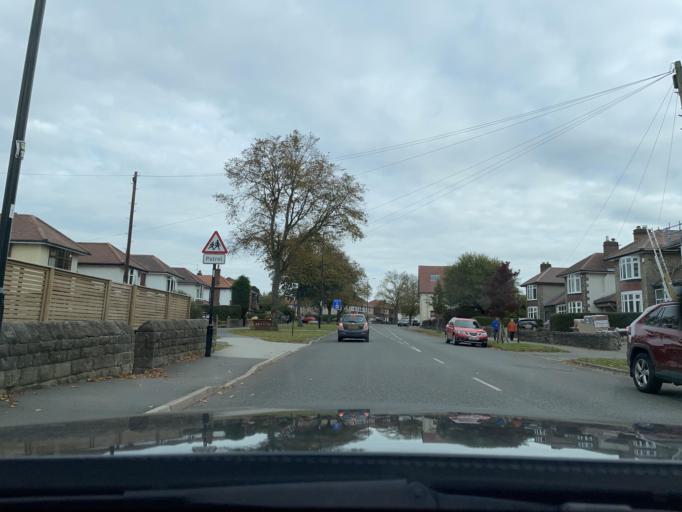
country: GB
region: England
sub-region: Sheffield
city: Oughtibridge
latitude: 53.3808
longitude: -1.5247
